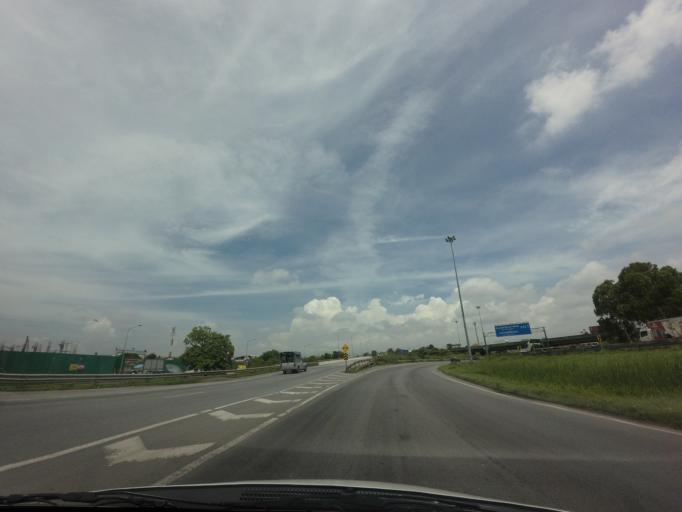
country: TH
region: Bangkok
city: Thung Khru
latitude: 13.6248
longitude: 100.5232
